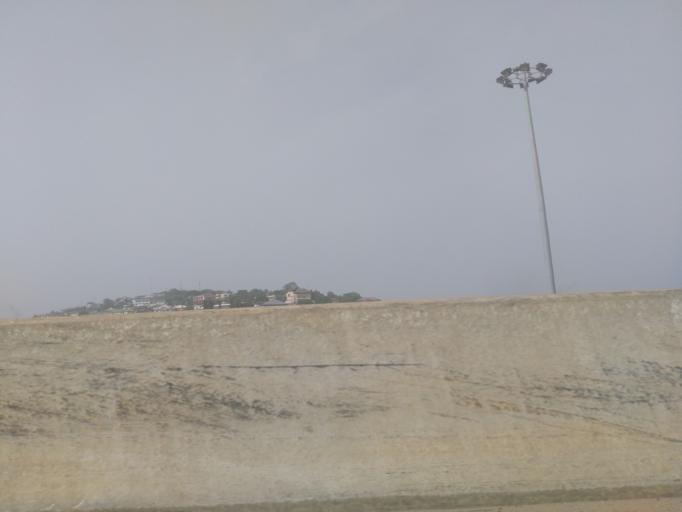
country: GH
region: Greater Accra
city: Gbawe
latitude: 5.5715
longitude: -0.2842
